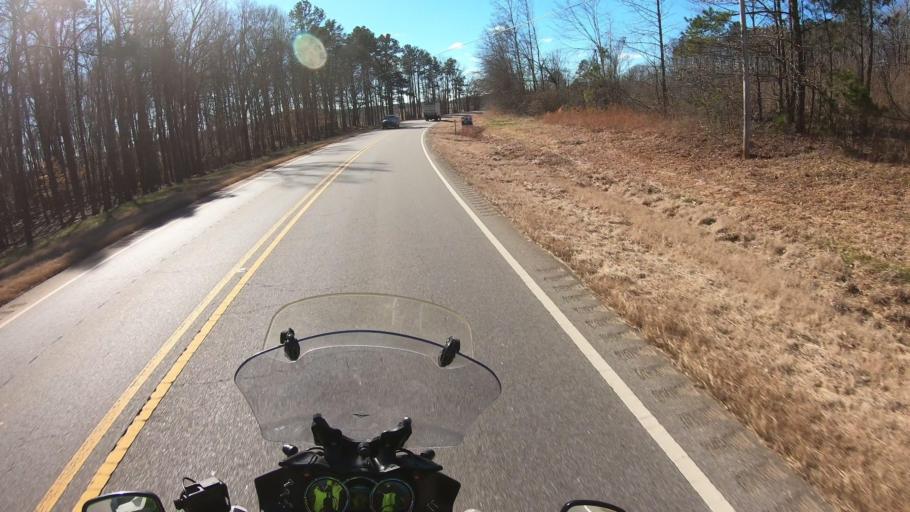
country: US
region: Alabama
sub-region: Cleburne County
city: Heflin
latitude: 33.5338
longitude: -85.6218
